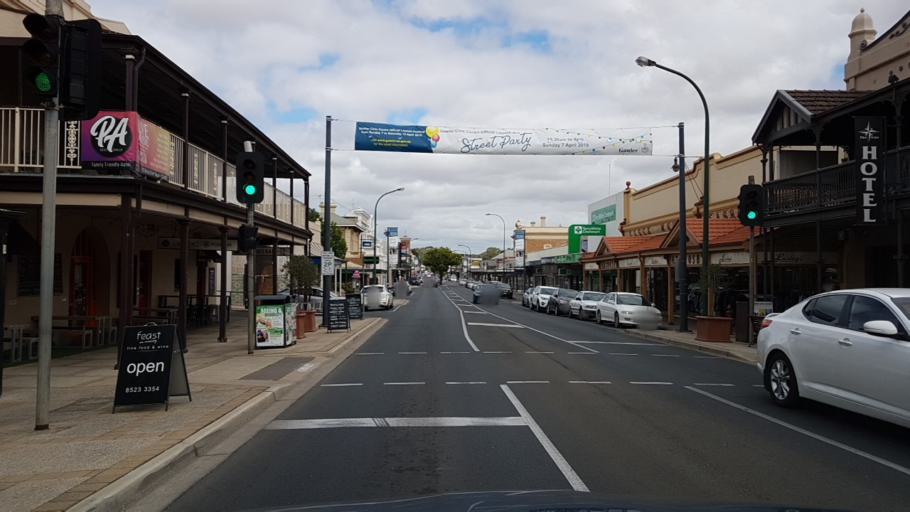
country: AU
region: South Australia
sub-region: Gawler
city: Gawler
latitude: -34.5982
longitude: 138.7491
